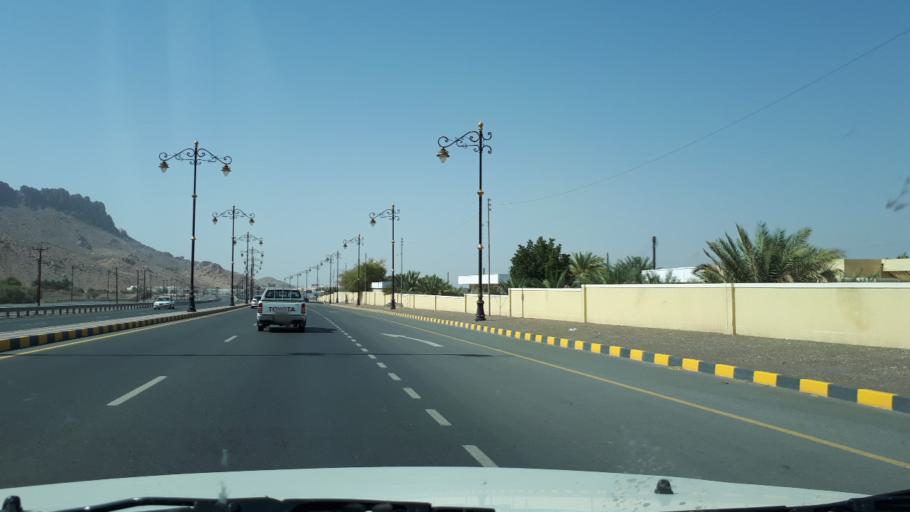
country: OM
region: Muhafazat ad Dakhiliyah
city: Nizwa
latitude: 22.9158
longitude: 57.5352
